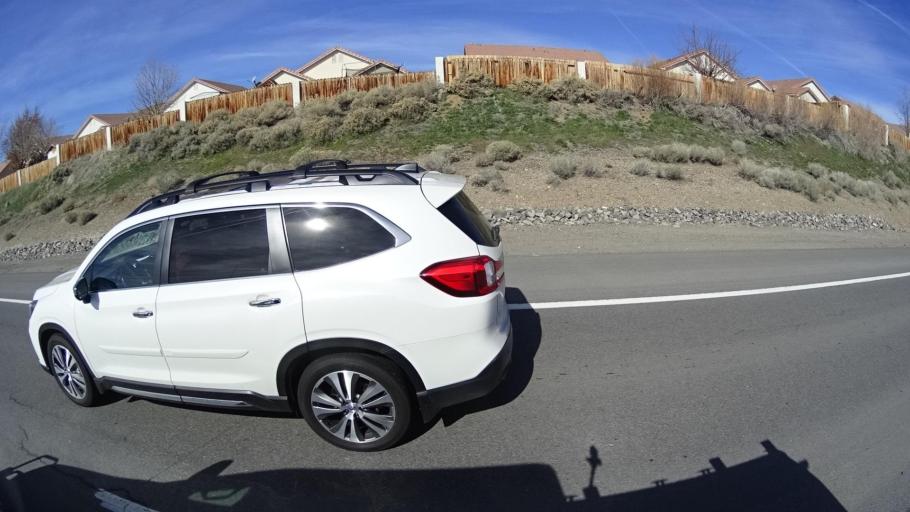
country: US
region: Nevada
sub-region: Washoe County
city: Sun Valley
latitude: 39.5887
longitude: -119.7409
